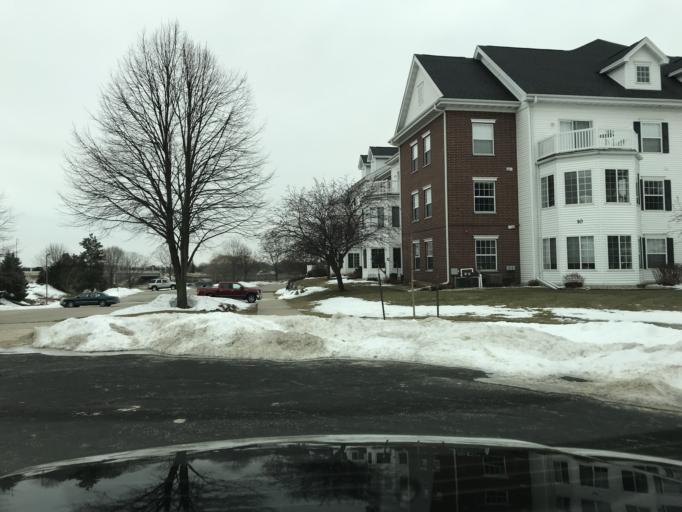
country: US
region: Wisconsin
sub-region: Dane County
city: Monona
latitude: 43.0765
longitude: -89.2785
